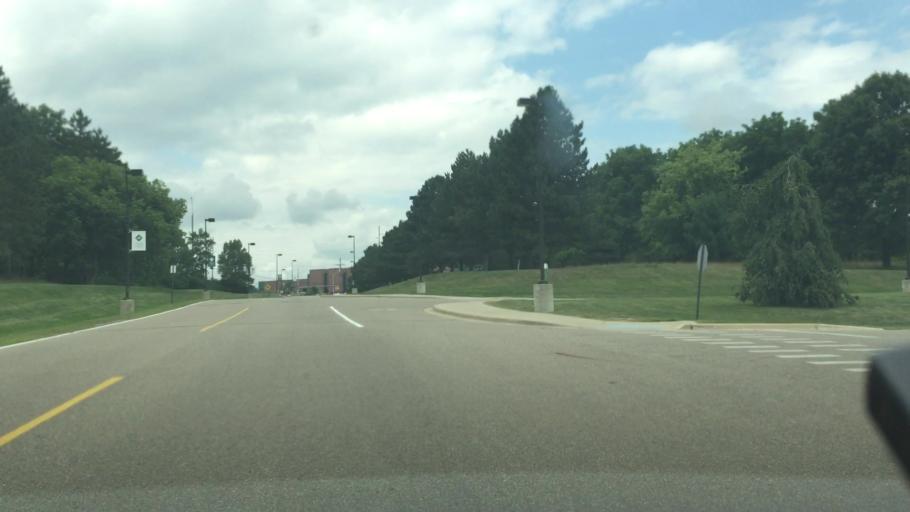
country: US
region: Michigan
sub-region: Oakland County
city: Auburn Hills
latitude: 42.6476
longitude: -83.2267
